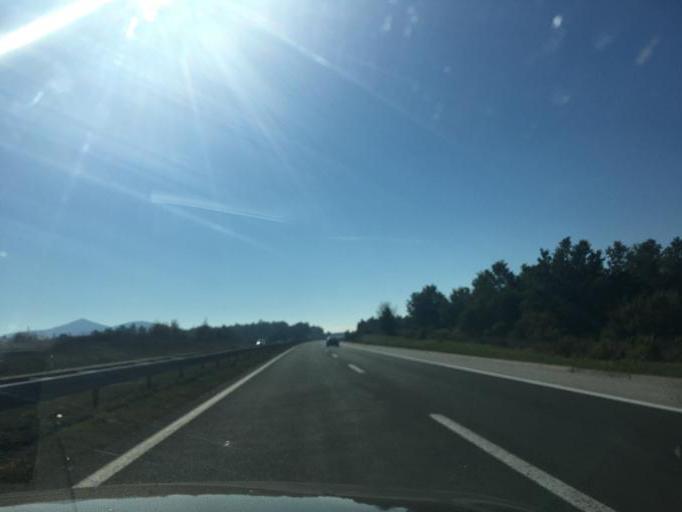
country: HR
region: Zadarska
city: Starigrad
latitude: 44.4539
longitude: 15.6107
